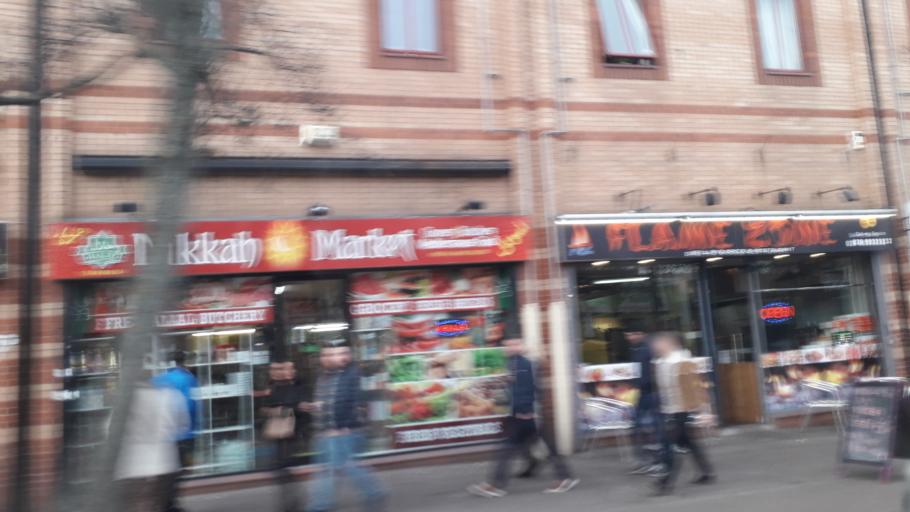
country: GB
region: Northern Ireland
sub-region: City of Belfast
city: Belfast
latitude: 54.5885
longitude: -5.9352
